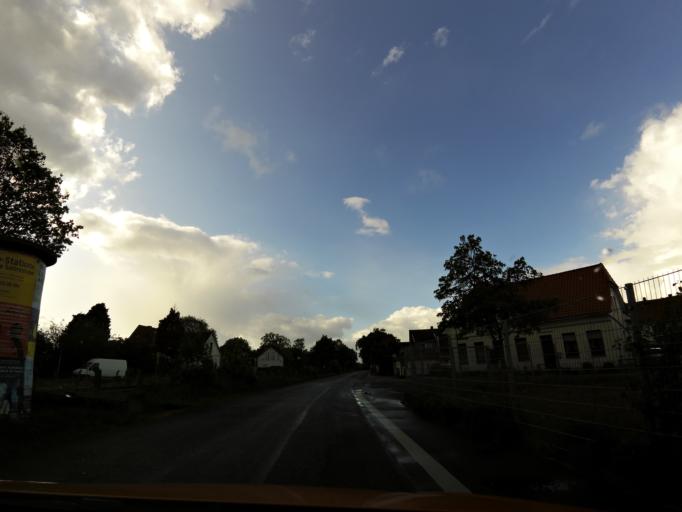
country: DE
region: Lower Saxony
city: Oldenburg
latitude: 53.1335
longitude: 8.2367
